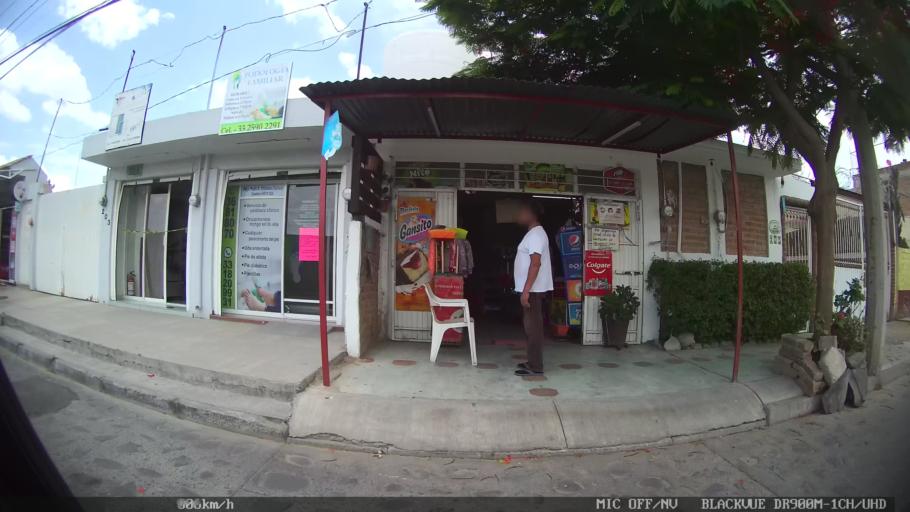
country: MX
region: Jalisco
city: Tonala
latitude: 20.6683
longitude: -103.2286
